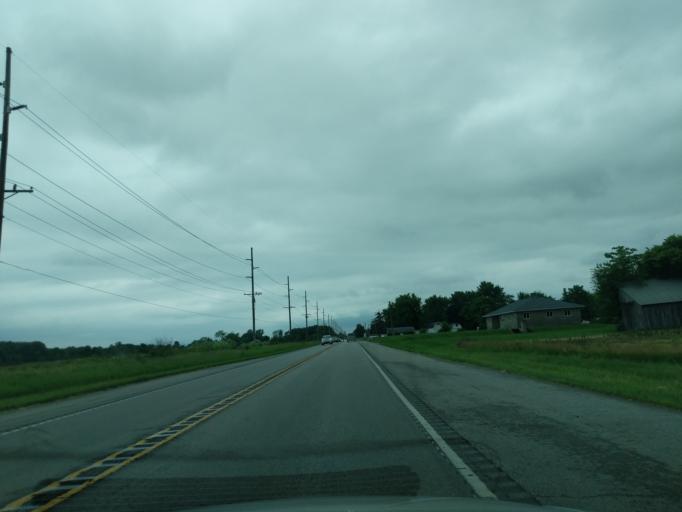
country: US
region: Indiana
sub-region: Hamilton County
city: Cicero
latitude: 40.0896
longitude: -86.0142
